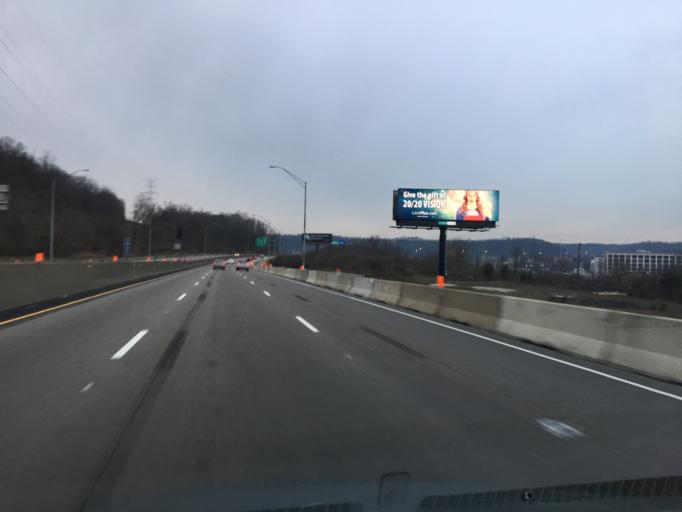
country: US
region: Ohio
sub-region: Hamilton County
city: Saint Bernard
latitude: 39.1591
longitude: -84.5282
